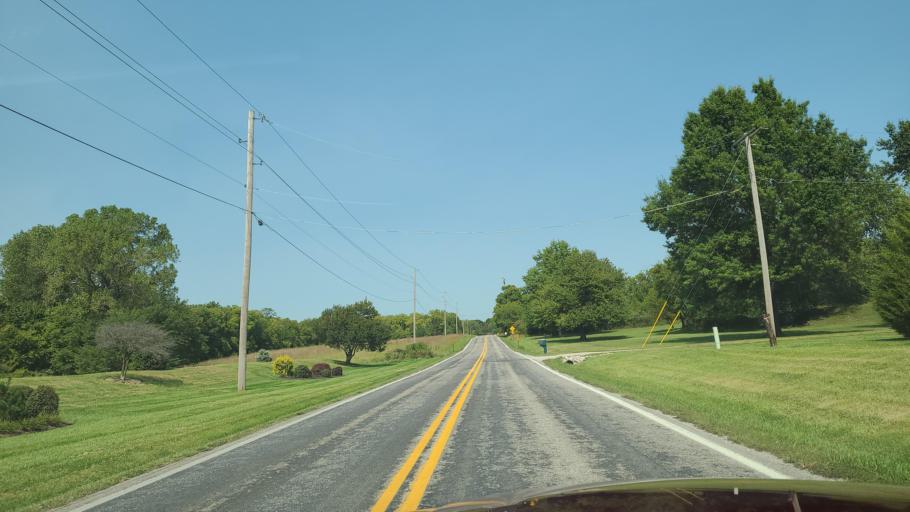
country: US
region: Kansas
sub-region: Douglas County
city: Lawrence
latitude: 38.9813
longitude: -95.2976
